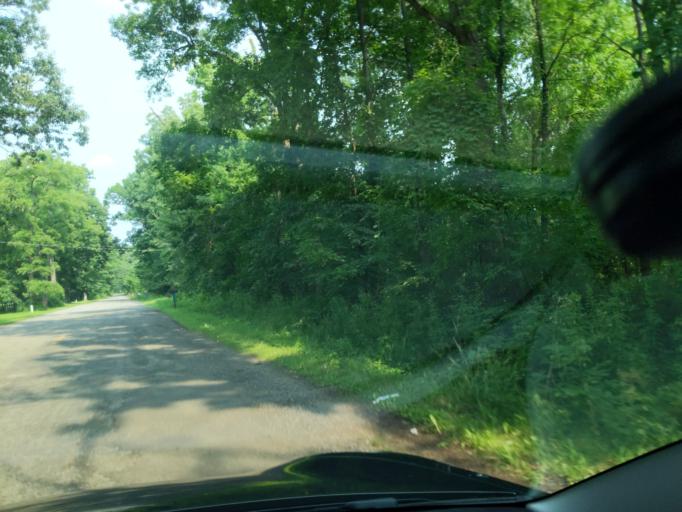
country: US
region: Michigan
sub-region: Ingham County
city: Leslie
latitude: 42.3899
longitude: -84.5489
